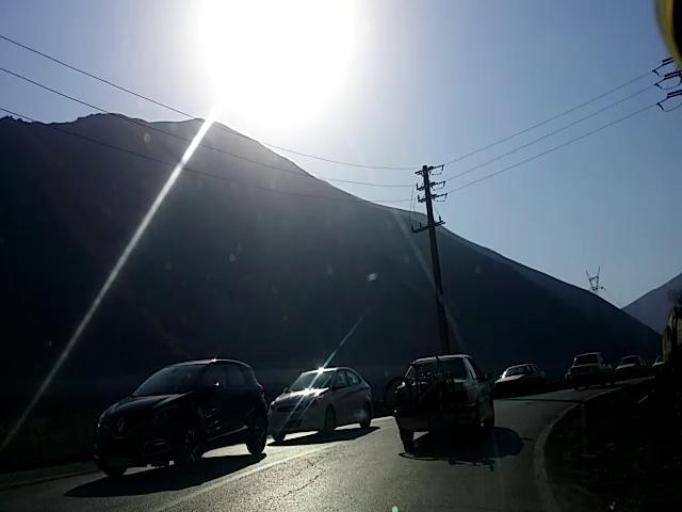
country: IR
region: Tehran
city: Tajrish
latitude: 36.1269
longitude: 51.3189
